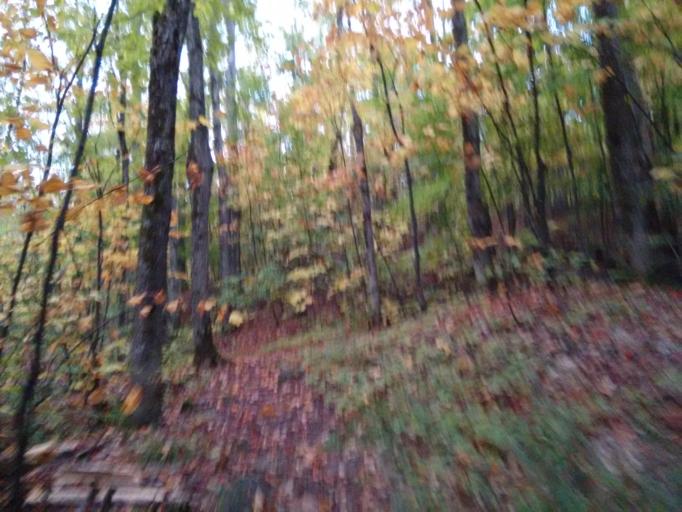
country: CA
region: Quebec
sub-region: Outaouais
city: Wakefield
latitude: 45.5337
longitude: -75.9201
